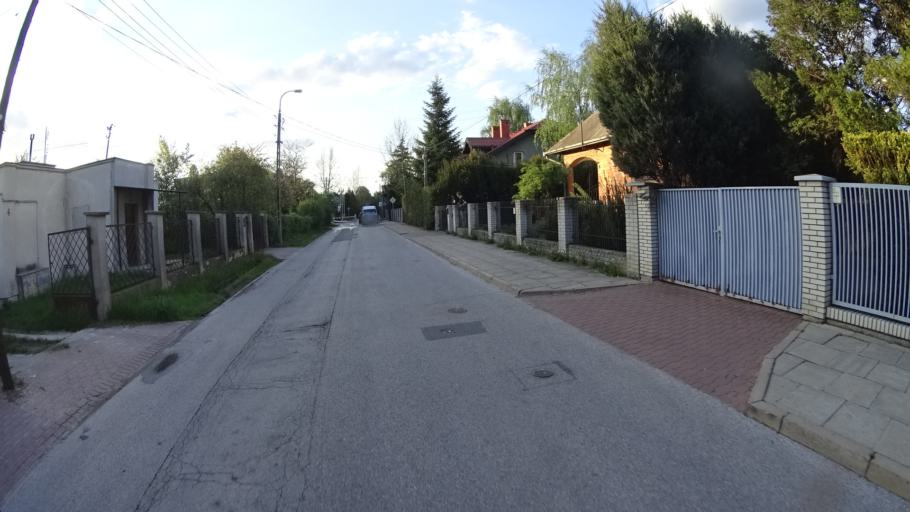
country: PL
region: Masovian Voivodeship
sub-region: Warszawa
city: Ursus
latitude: 52.2039
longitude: 20.8595
